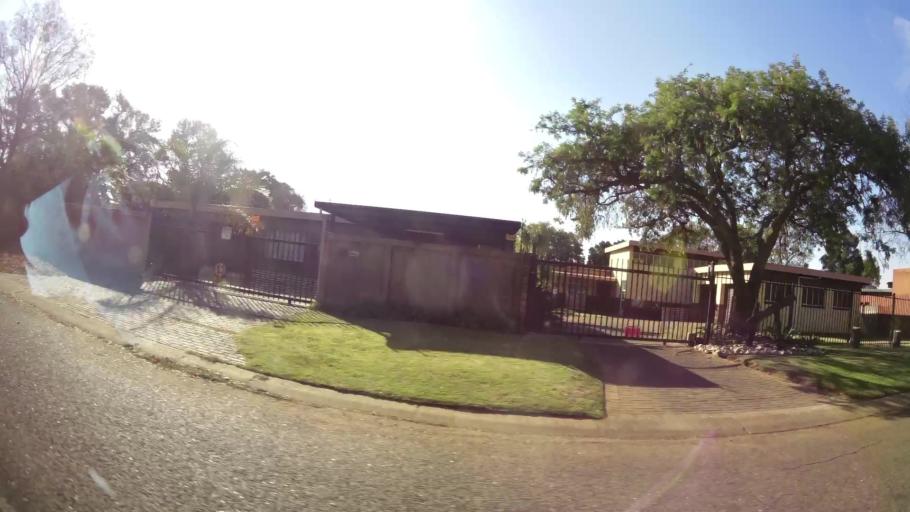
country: ZA
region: Gauteng
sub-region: City of Tshwane Metropolitan Municipality
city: Pretoria
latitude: -25.7232
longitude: 28.2588
